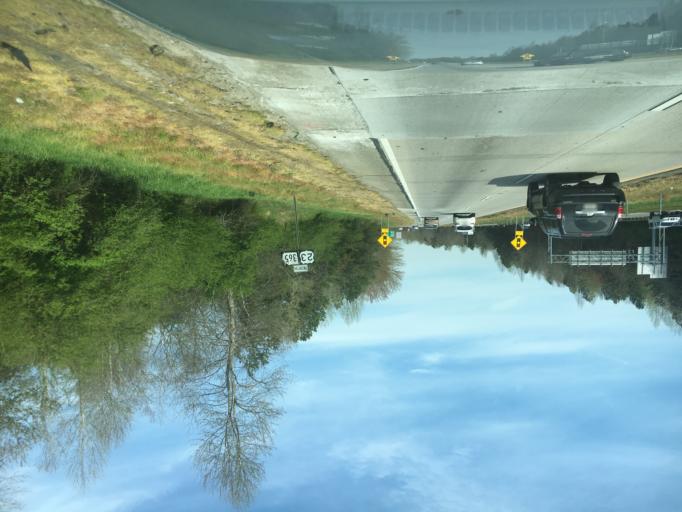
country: US
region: Georgia
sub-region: Hall County
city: Gainesville
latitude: 34.3244
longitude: -83.7868
